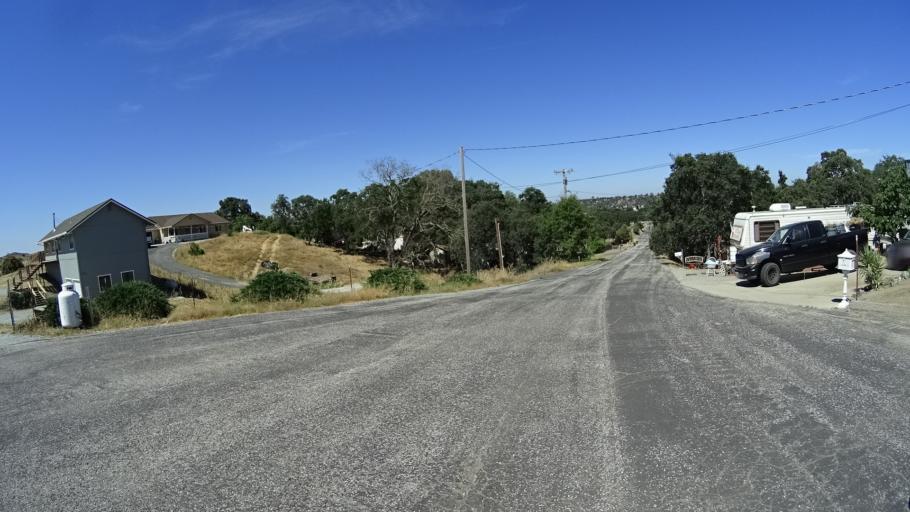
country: US
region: California
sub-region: Calaveras County
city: Valley Springs
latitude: 38.1591
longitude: -120.8308
